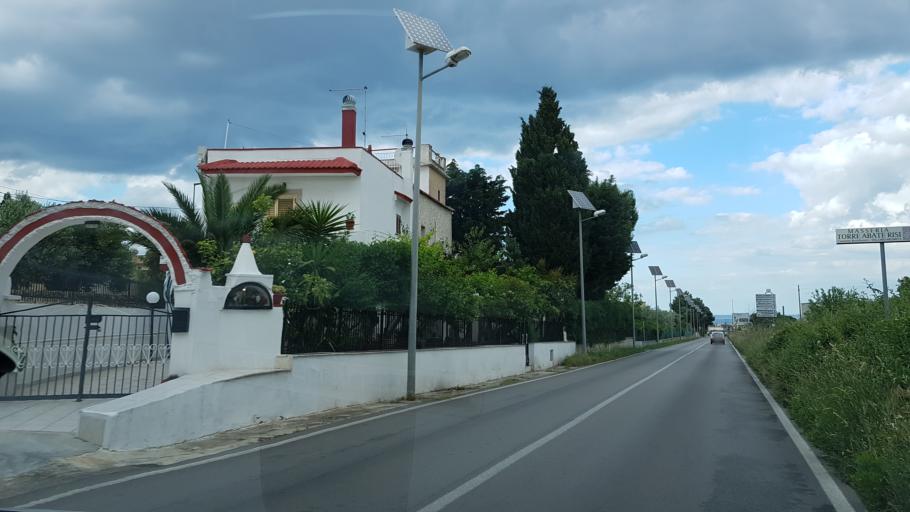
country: IT
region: Apulia
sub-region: Provincia di Brindisi
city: Fasano
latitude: 40.8472
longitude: 17.3833
